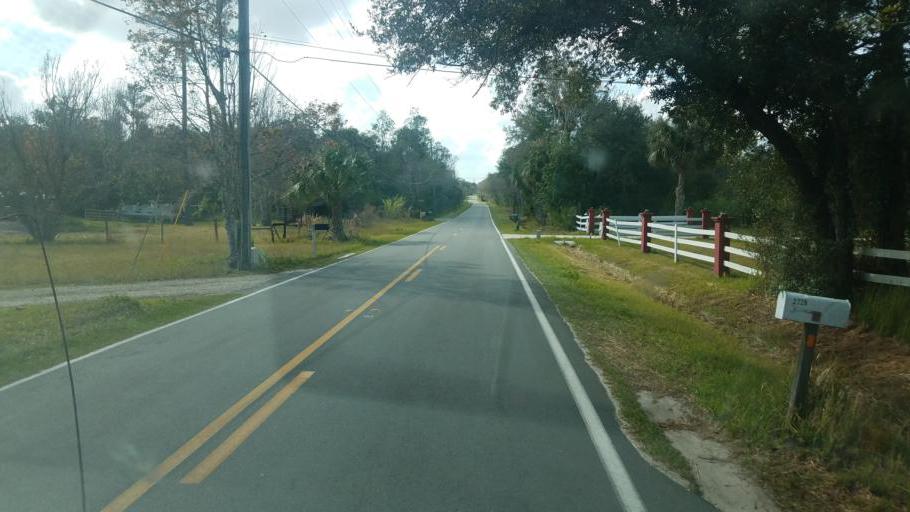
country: US
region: Florida
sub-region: Polk County
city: Davenport
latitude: 28.1468
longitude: -81.5688
